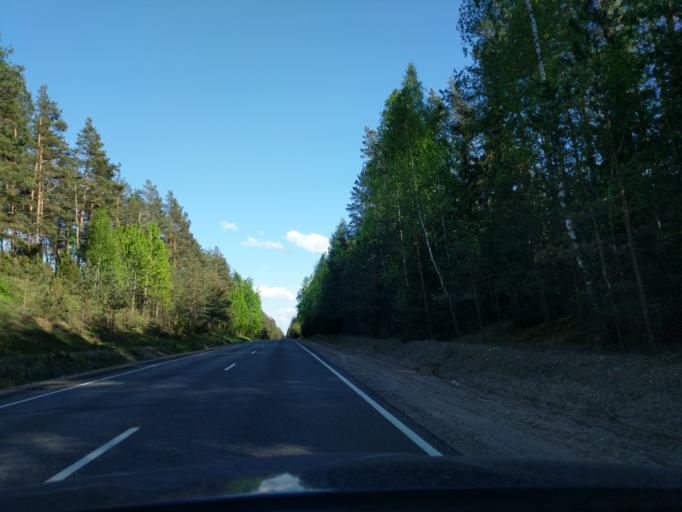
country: BY
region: Minsk
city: Myadzyel
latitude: 54.8103
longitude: 26.9814
